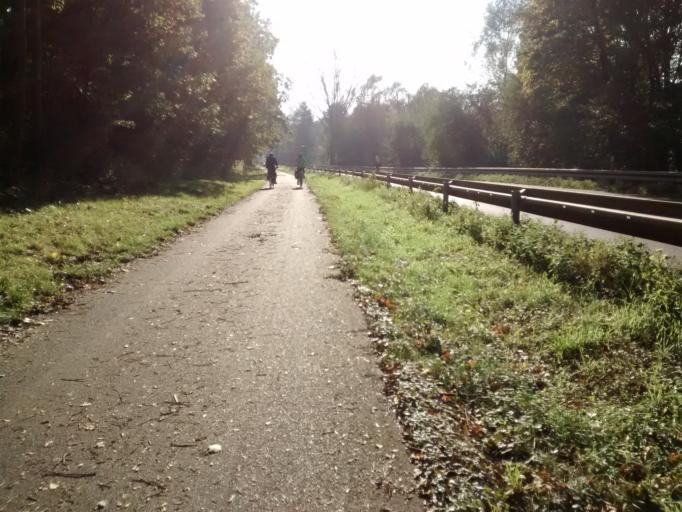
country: DE
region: Brandenburg
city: Hennigsdorf
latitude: 52.6415
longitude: 13.2240
